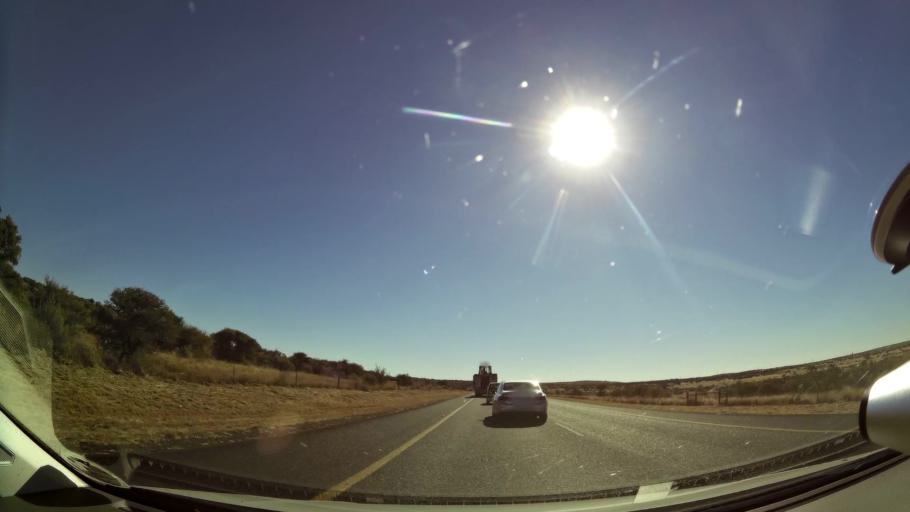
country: ZA
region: Northern Cape
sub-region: Frances Baard District Municipality
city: Warrenton
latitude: -28.3173
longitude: 24.8260
